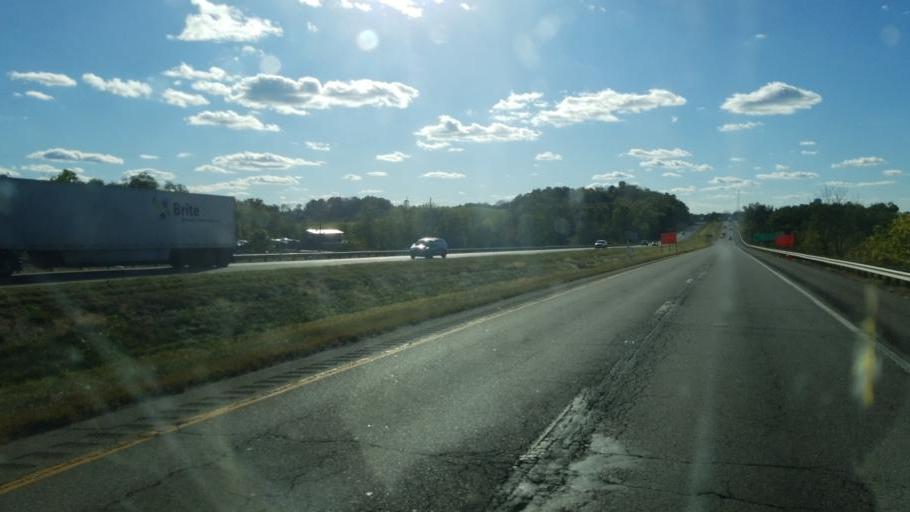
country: US
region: Ohio
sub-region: Belmont County
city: Saint Clairsville
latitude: 40.0780
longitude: -80.9473
